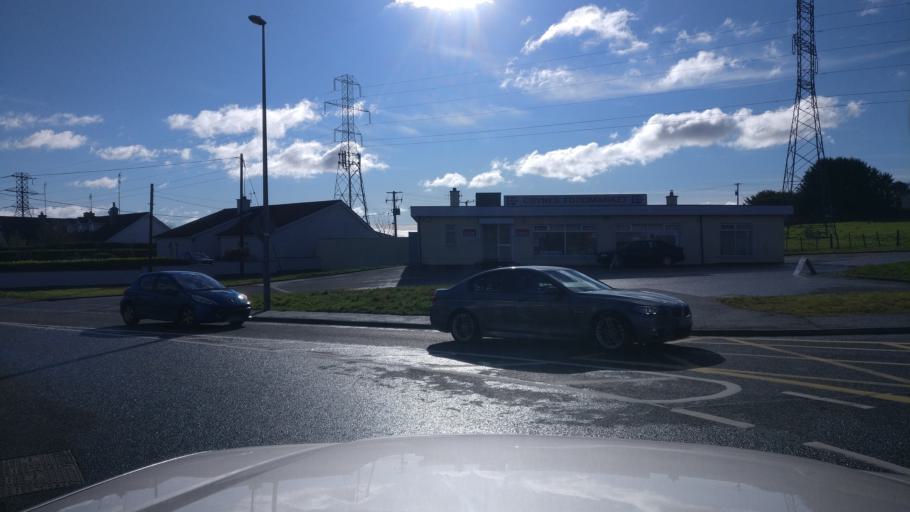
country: IE
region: Connaught
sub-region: County Galway
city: Gaillimh
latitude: 53.2908
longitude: -8.9885
